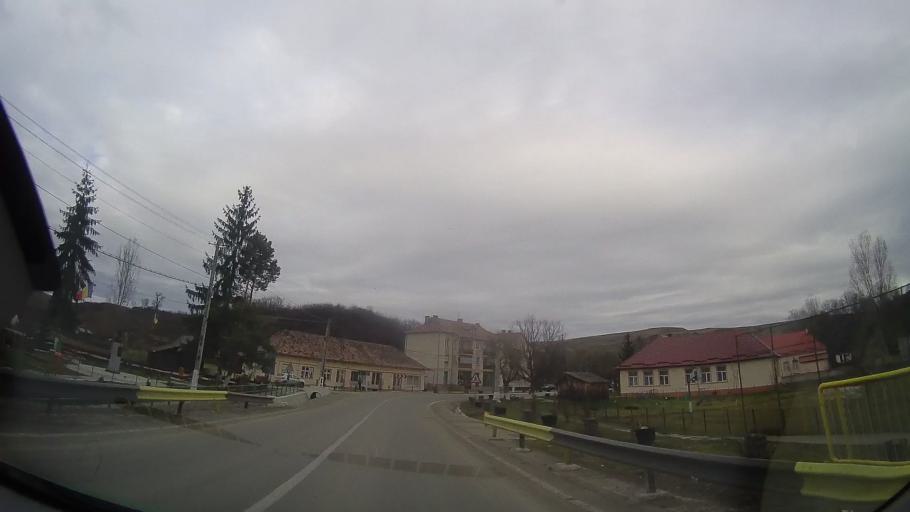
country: RO
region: Mures
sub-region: Comuna Faragau
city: Faragau
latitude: 46.7640
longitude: 24.5162
